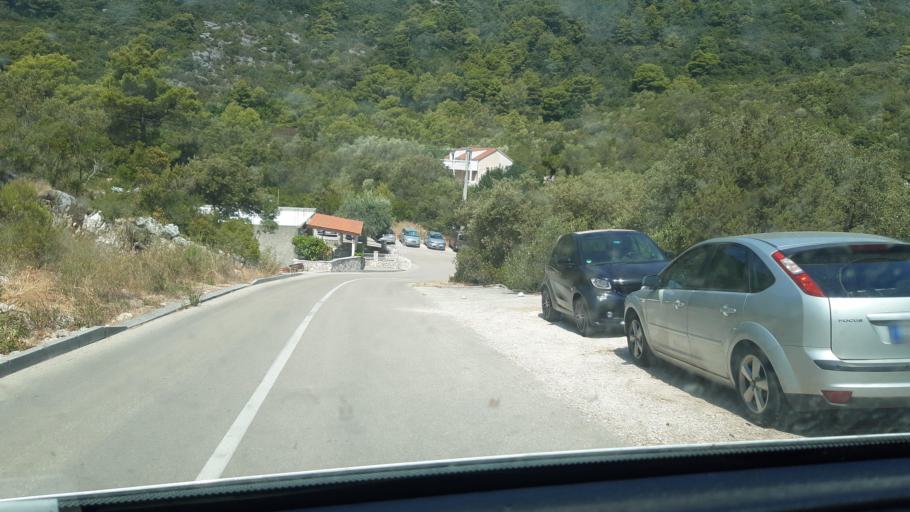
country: HR
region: Dubrovacko-Neretvanska
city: Ston
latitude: 42.7256
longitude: 17.6681
